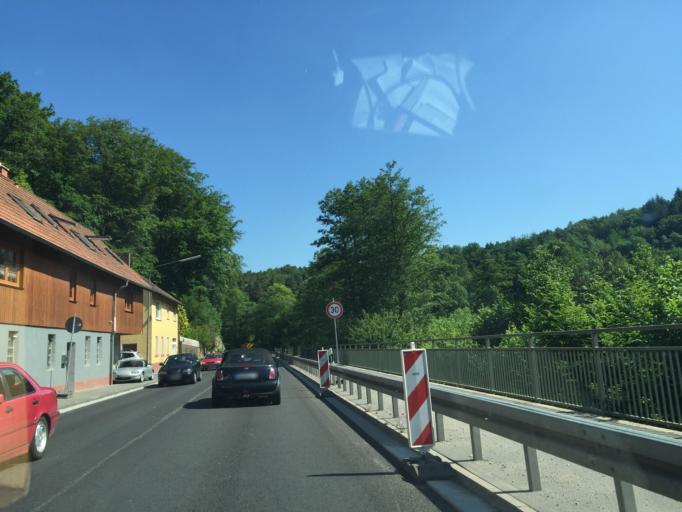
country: DE
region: Hesse
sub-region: Regierungsbezirk Darmstadt
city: Erbach
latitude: 49.6196
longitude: 8.9946
